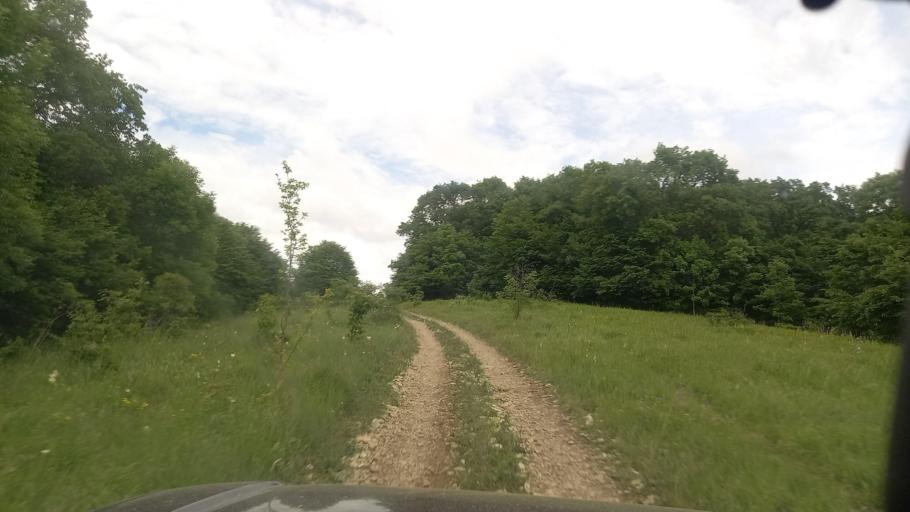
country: RU
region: Karachayevo-Cherkesiya
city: Pregradnaya
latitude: 44.0293
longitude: 41.3057
